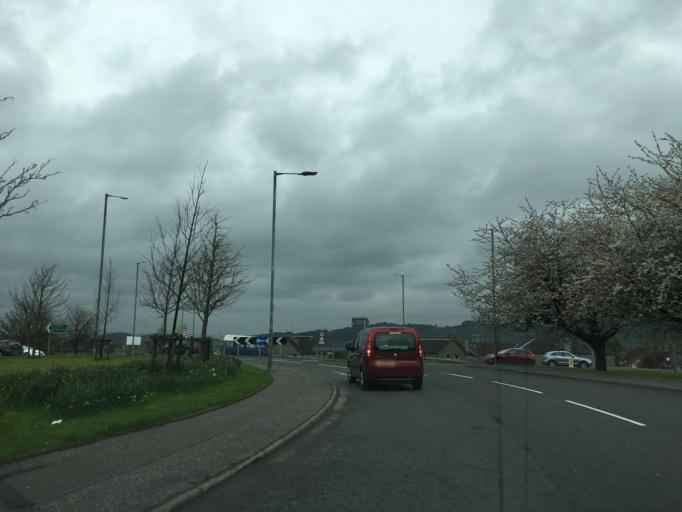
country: GB
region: Scotland
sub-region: Stirling
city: Stirling
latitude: 56.1277
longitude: -3.9408
